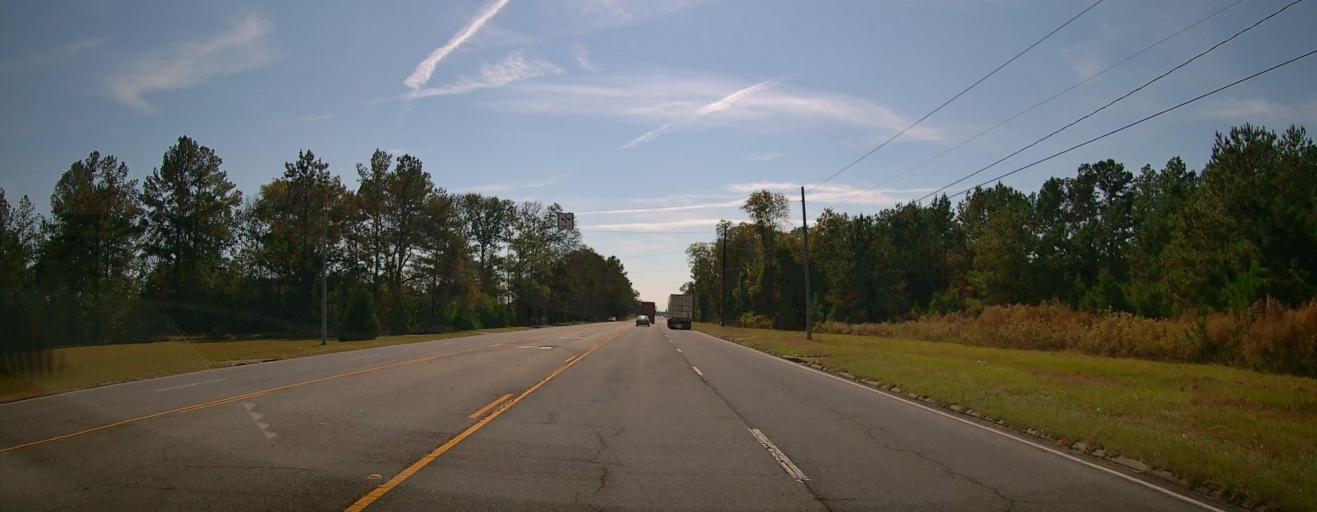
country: US
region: Georgia
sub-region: Lee County
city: Leesburg
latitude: 31.7837
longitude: -83.9647
